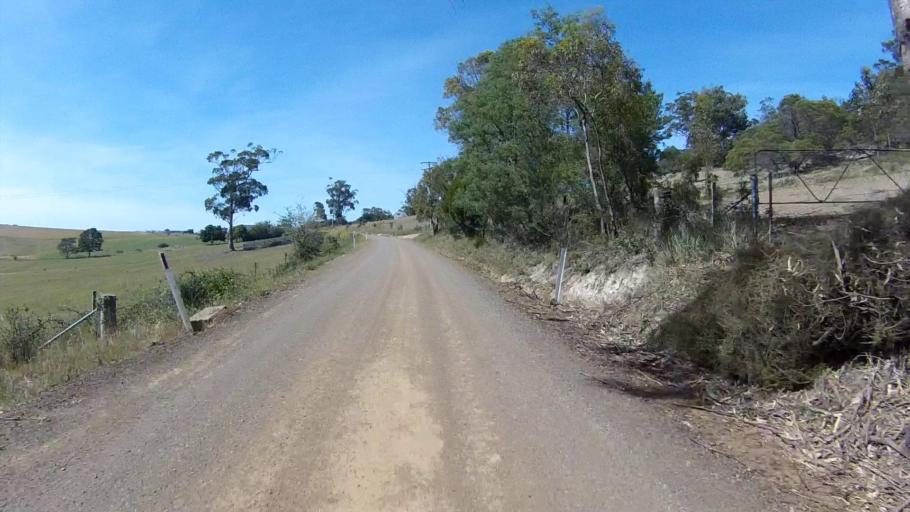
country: AU
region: Tasmania
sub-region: Sorell
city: Sorell
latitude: -42.7389
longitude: 147.5983
